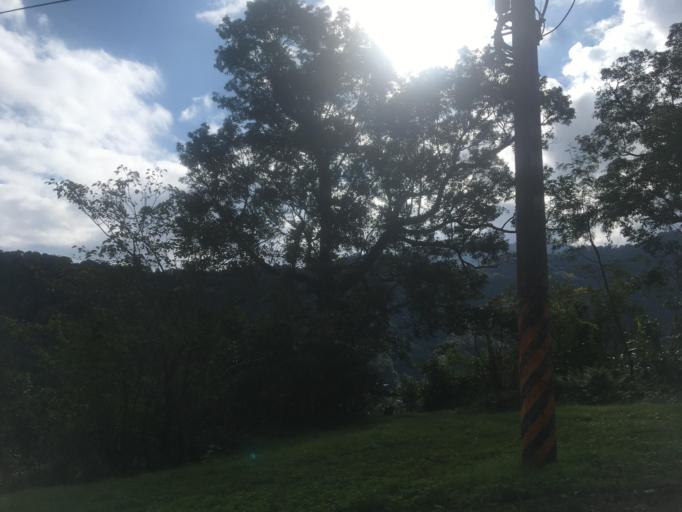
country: TW
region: Taiwan
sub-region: Yilan
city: Yilan
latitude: 24.6339
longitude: 121.5514
